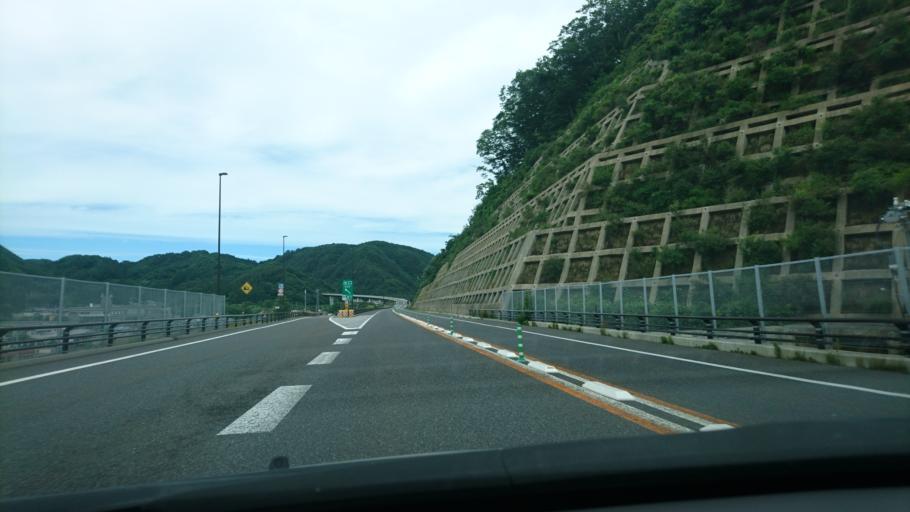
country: JP
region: Iwate
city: Miyako
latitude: 40.0010
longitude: 141.8864
